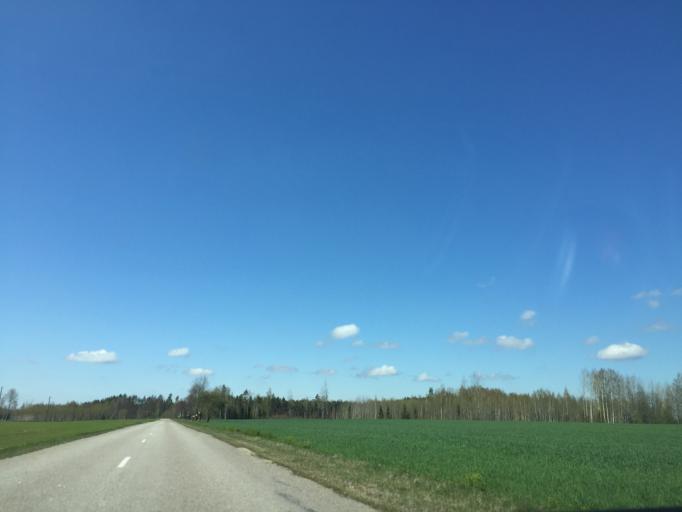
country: LV
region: Strenci
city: Seda
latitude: 57.5684
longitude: 25.8085
